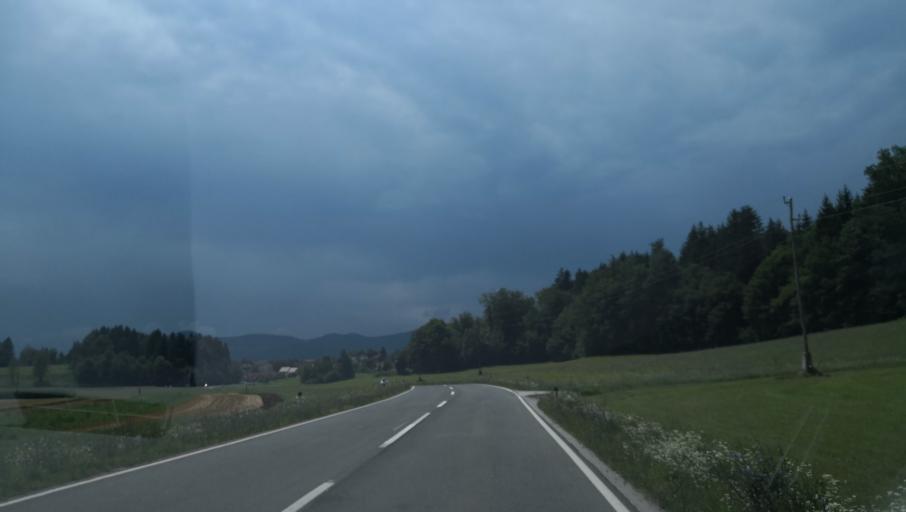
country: SI
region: Ivancna Gorica
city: Ivancna Gorica
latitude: 45.9112
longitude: 14.8008
